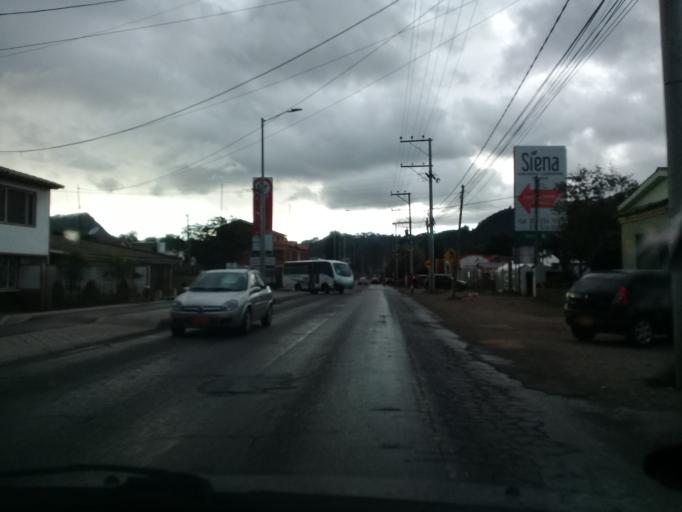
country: CO
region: Cundinamarca
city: Cajica
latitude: 4.9236
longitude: -74.0417
